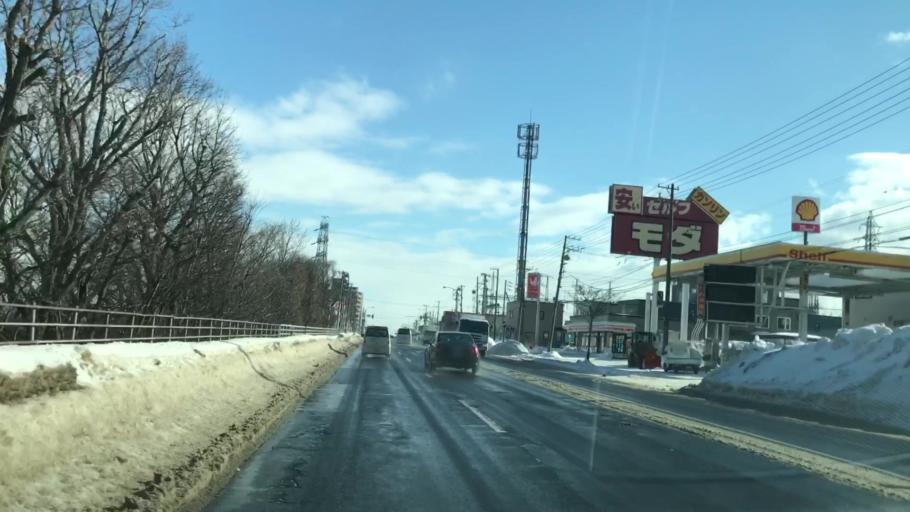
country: JP
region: Hokkaido
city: Sapporo
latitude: 43.1316
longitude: 141.2024
